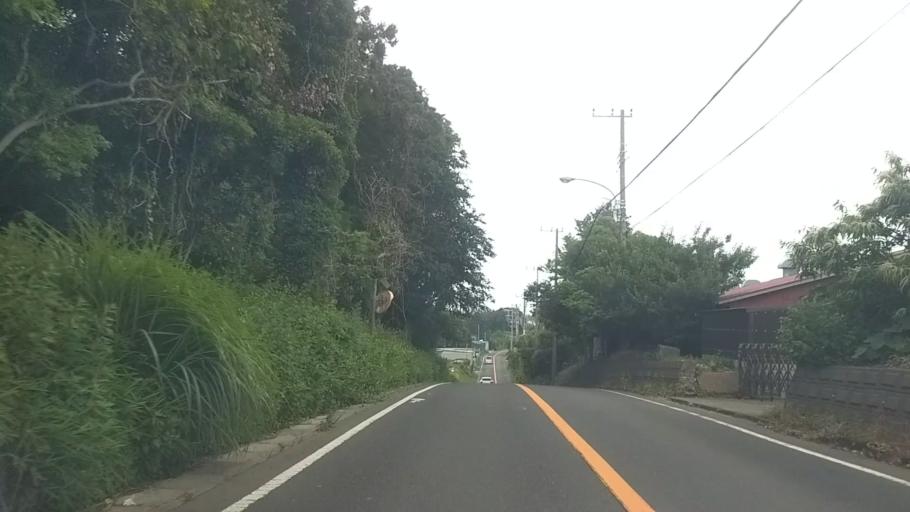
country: JP
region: Kanagawa
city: Fujisawa
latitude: 35.3539
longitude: 139.4352
